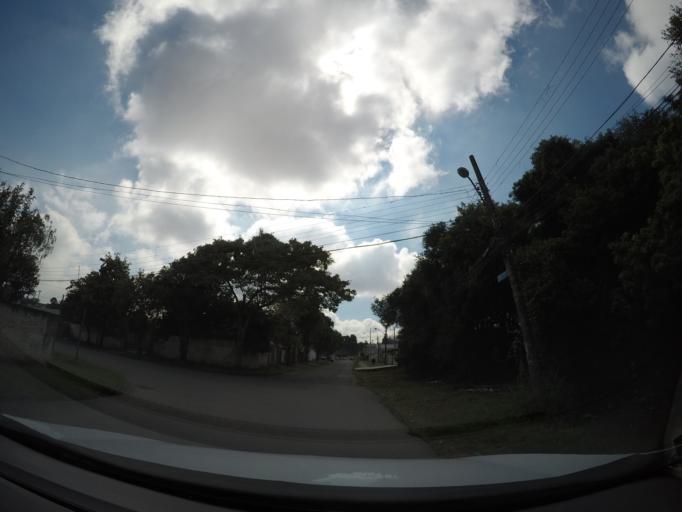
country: BR
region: Parana
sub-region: Sao Jose Dos Pinhais
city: Sao Jose dos Pinhais
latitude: -25.4931
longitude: -49.2264
